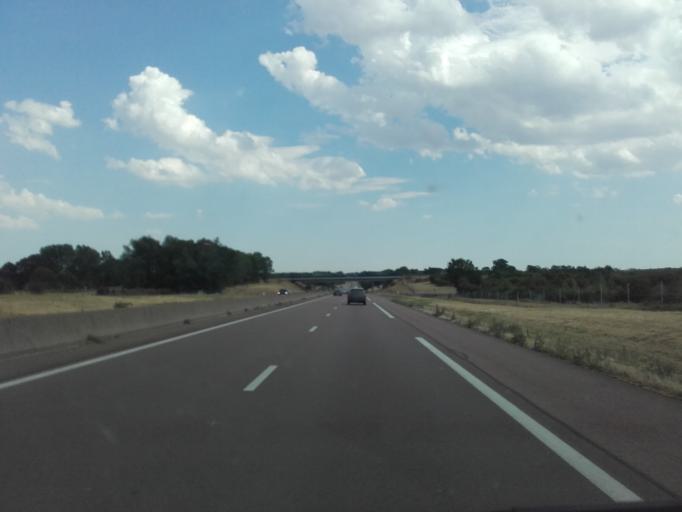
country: FR
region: Bourgogne
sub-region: Departement de l'Yonne
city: Avallon
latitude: 47.4991
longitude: 4.1113
